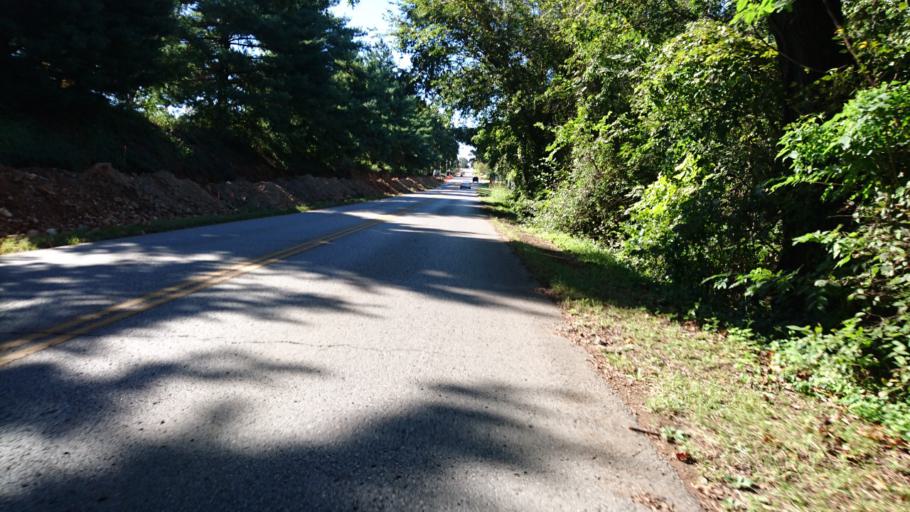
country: US
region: Missouri
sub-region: Jasper County
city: Joplin
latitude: 37.0968
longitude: -94.4946
